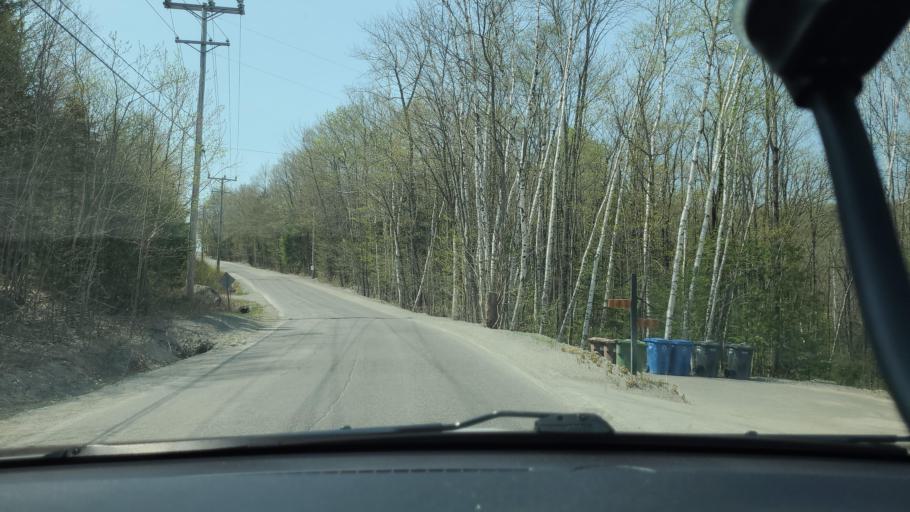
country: CA
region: Quebec
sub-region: Laurentides
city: Prevost
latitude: 45.9056
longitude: -74.0168
